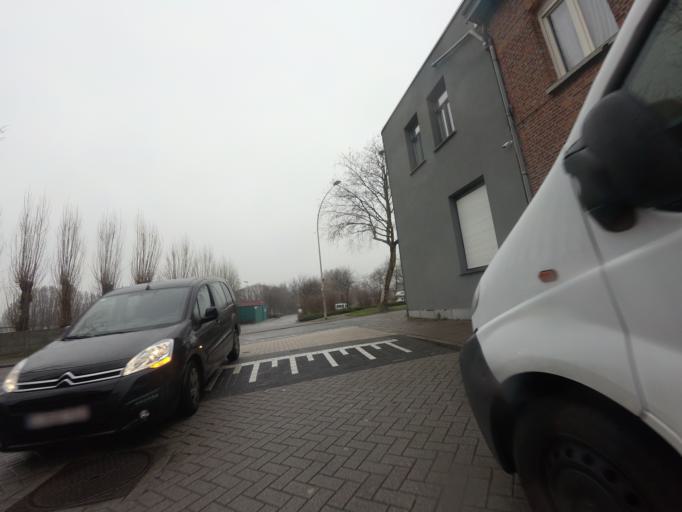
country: BE
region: Flanders
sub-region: Provincie Antwerpen
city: Hoboken
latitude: 51.1776
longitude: 4.3437
